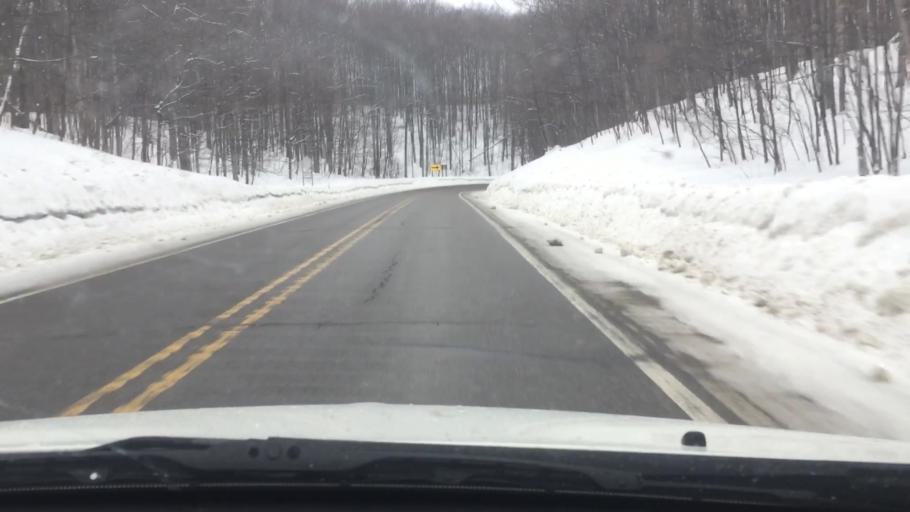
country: US
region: Michigan
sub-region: Charlevoix County
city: Boyne City
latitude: 45.0791
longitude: -84.9104
